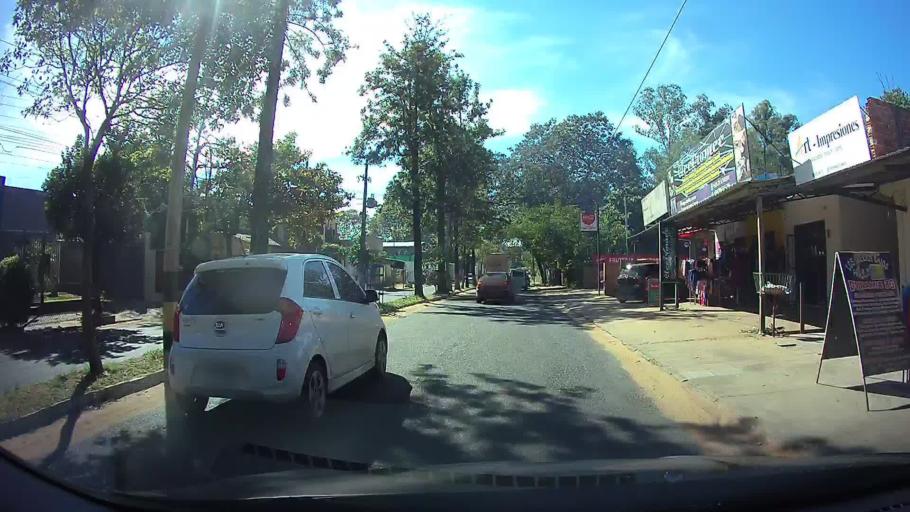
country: PY
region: Central
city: Villa Elisa
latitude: -25.3595
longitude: -57.5737
